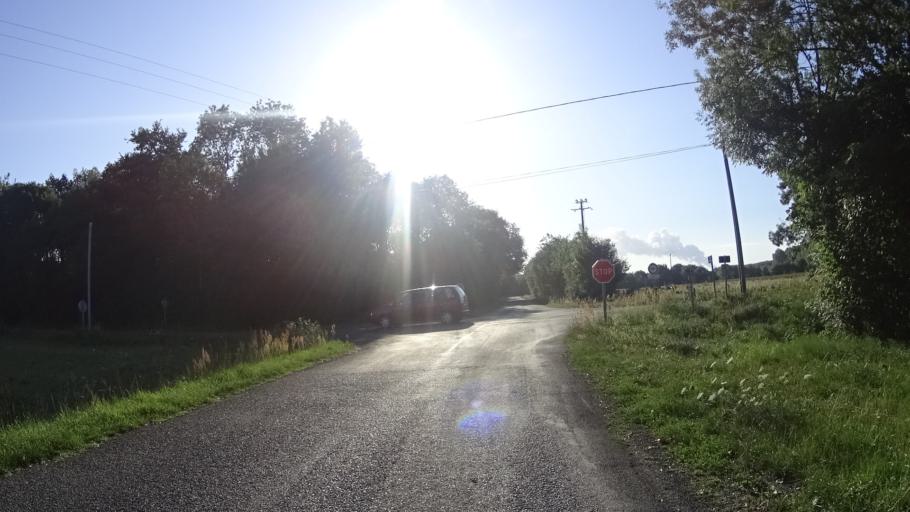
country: FR
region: Pays de la Loire
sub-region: Departement de Maine-et-Loire
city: Allonnes
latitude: 47.2706
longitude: 0.0045
